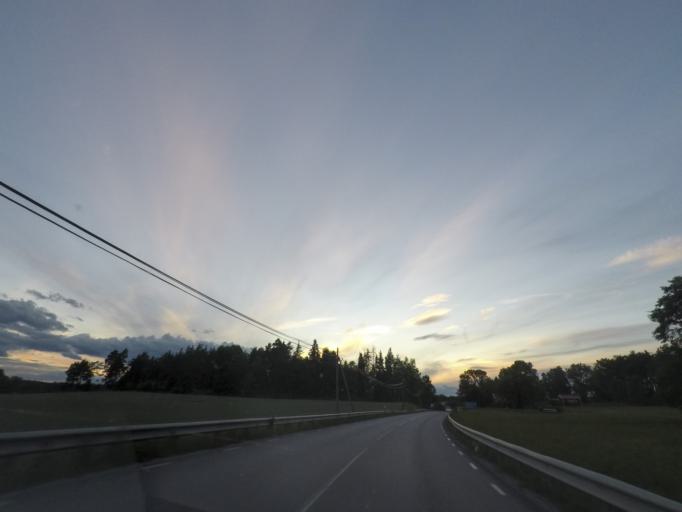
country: SE
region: Stockholm
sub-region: Sigtuna Kommun
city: Sigtuna
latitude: 59.6560
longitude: 17.6934
